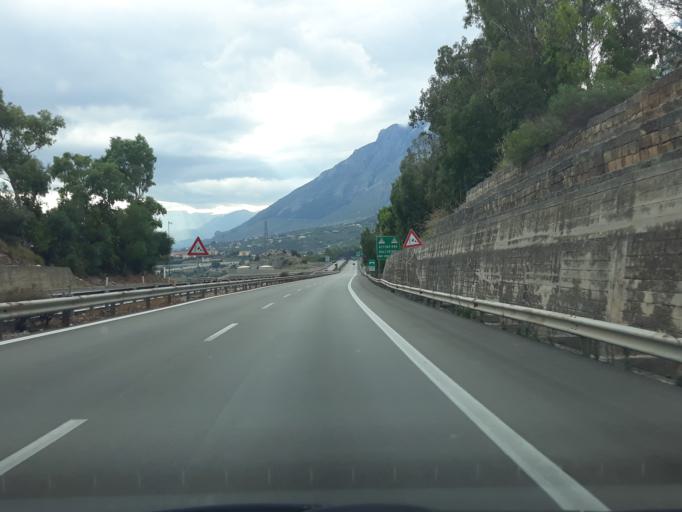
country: IT
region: Sicily
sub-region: Palermo
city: Termini Imerese
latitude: 37.9815
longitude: 13.6678
